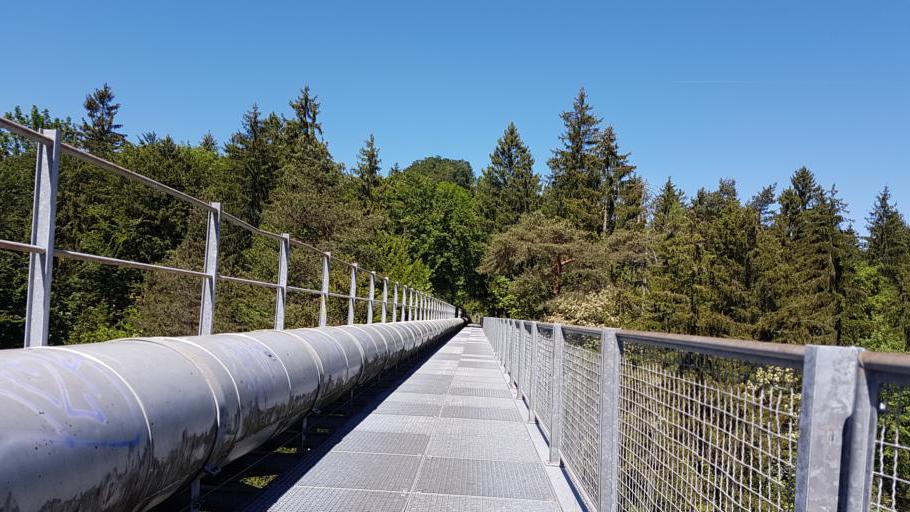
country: CH
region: Bern
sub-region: Frutigen-Niedersimmental District
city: Wimmis
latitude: 46.7045
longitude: 7.6338
